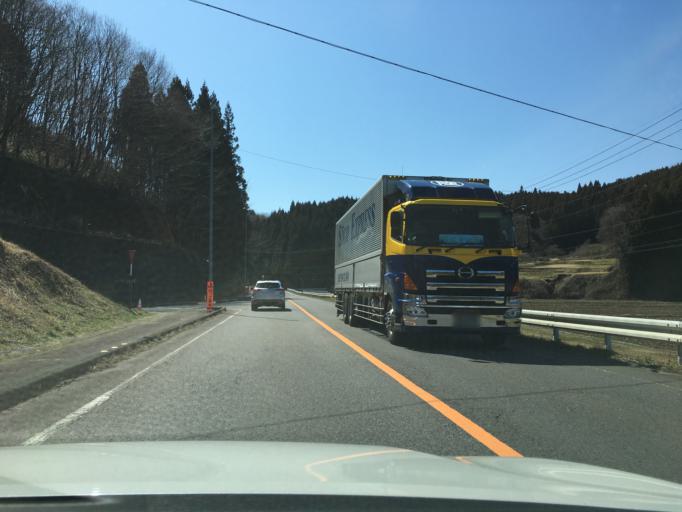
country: JP
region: Tochigi
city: Kuroiso
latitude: 37.0549
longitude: 140.1720
